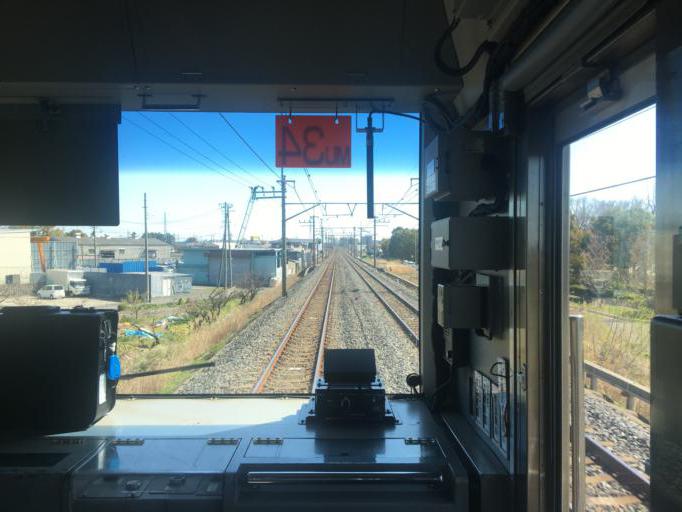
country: JP
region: Saitama
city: Koshigaya
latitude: 35.8755
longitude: 139.7661
